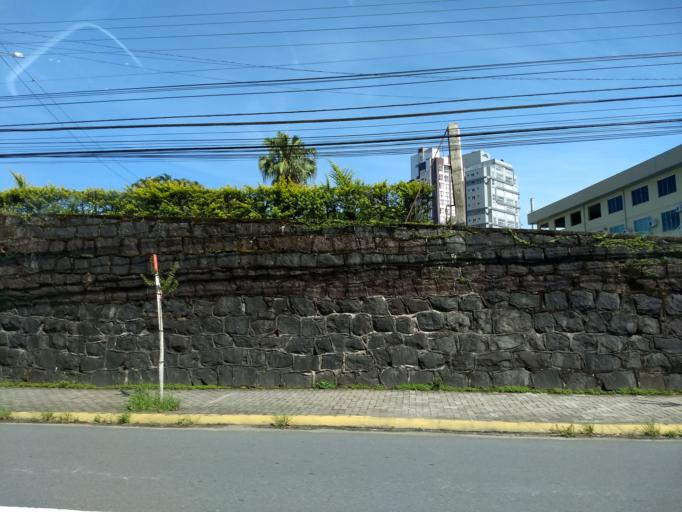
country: BR
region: Santa Catarina
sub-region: Jaragua Do Sul
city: Jaragua do Sul
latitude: -26.4923
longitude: -49.0840
